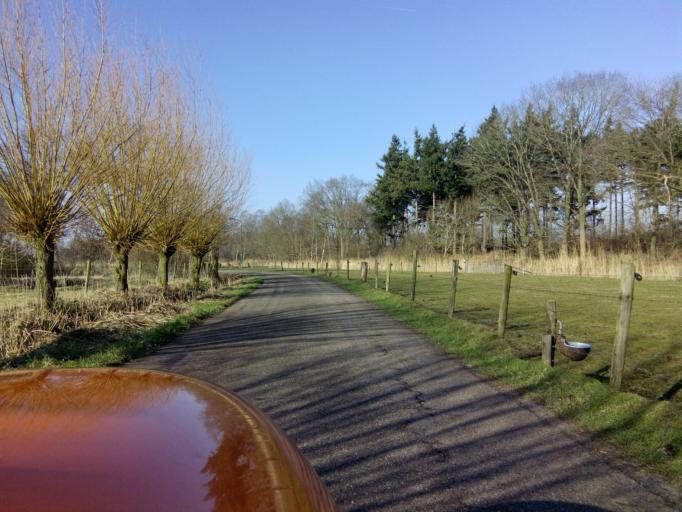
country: NL
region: Gelderland
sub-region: Gemeente Barneveld
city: Terschuur
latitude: 52.1133
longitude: 5.4929
